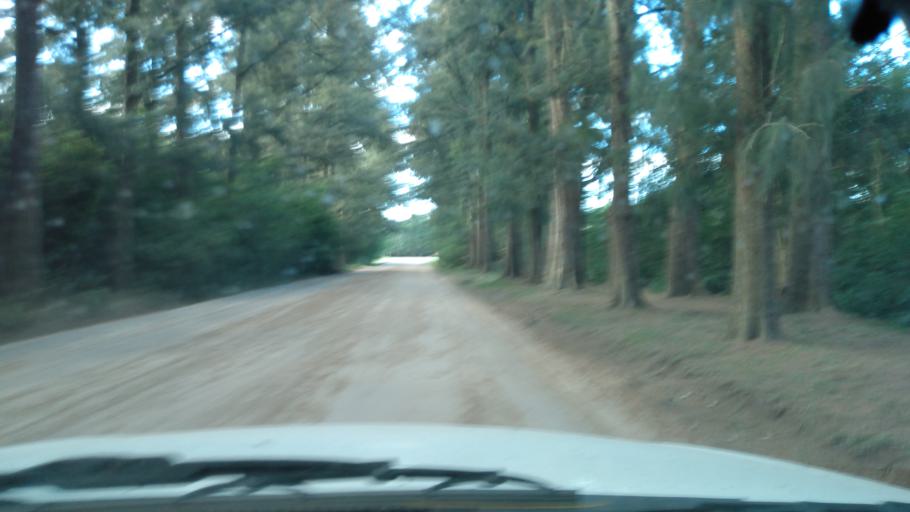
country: AR
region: Buenos Aires
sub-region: Partido de Lujan
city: Lujan
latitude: -34.5485
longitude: -59.1612
